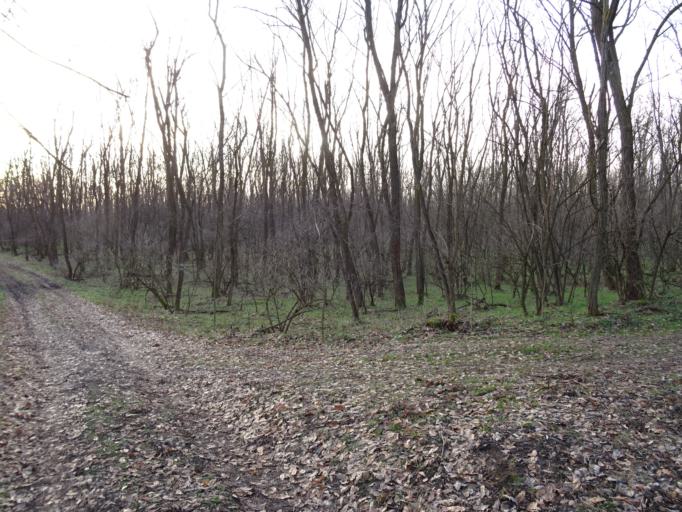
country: HU
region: Pest
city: Mende
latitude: 47.4084
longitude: 19.4427
